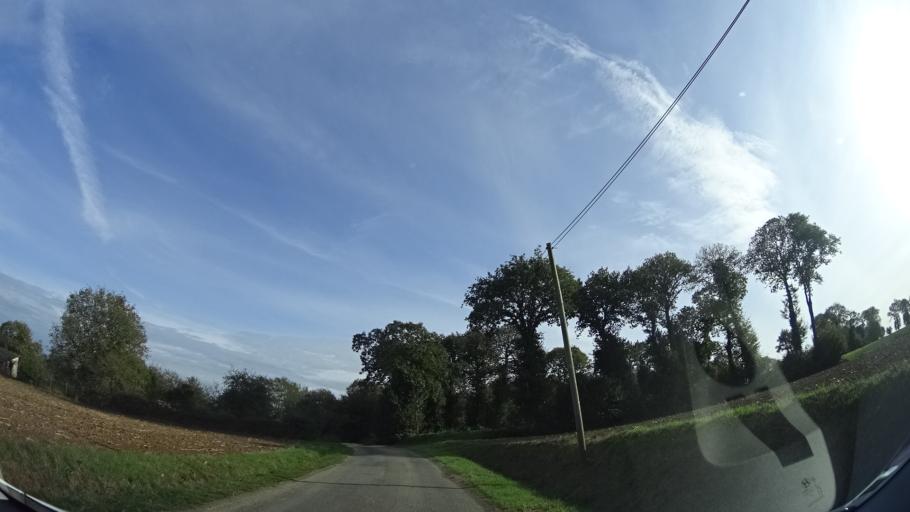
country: FR
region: Brittany
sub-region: Departement d'Ille-et-Vilaine
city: Geveze
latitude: 48.2306
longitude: -1.8042
